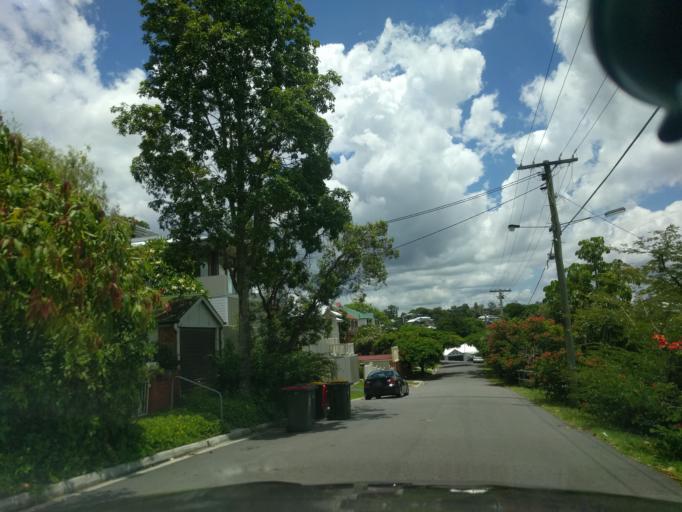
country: AU
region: Queensland
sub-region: Brisbane
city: Milton
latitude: -27.4725
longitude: 152.9962
